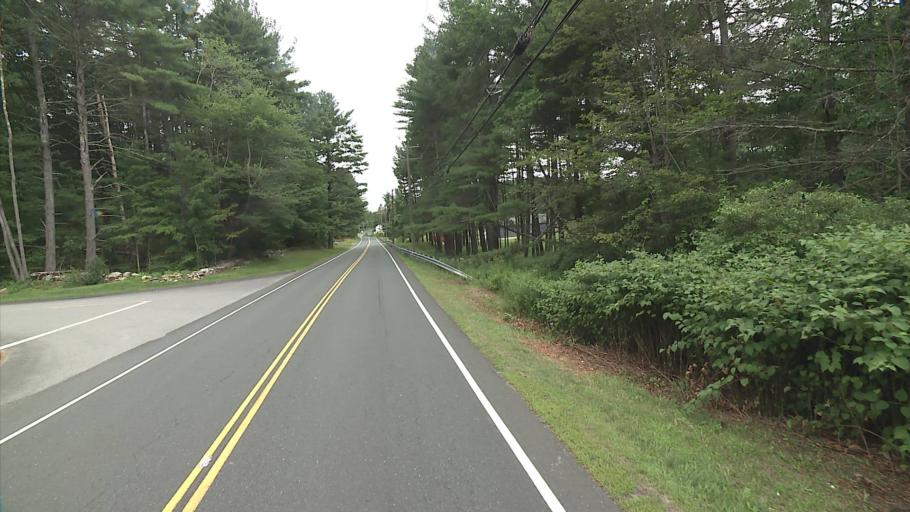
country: US
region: Connecticut
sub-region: Litchfield County
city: Winsted
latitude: 41.9561
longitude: -73.0484
